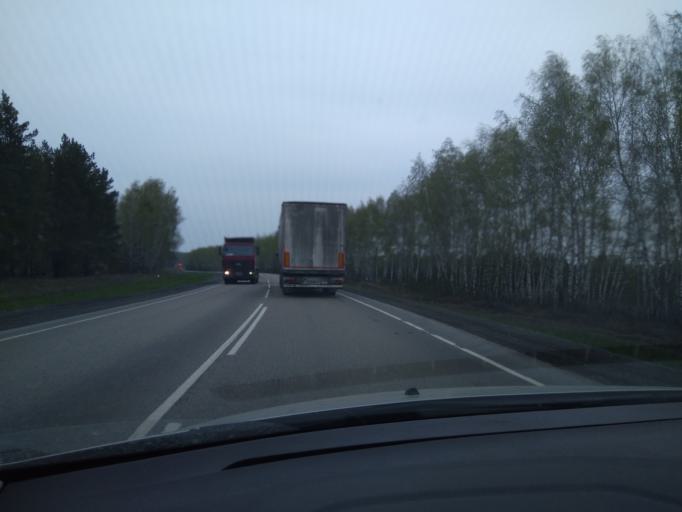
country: RU
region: Sverdlovsk
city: Zarechnyy
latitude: 56.7414
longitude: 61.2693
